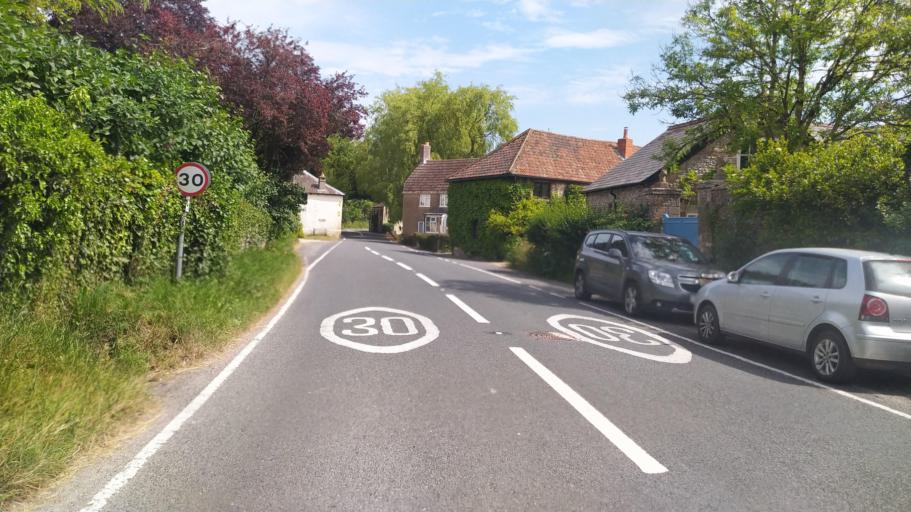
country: GB
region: England
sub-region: Dorset
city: Dorchester
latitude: 50.7741
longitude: -2.4738
